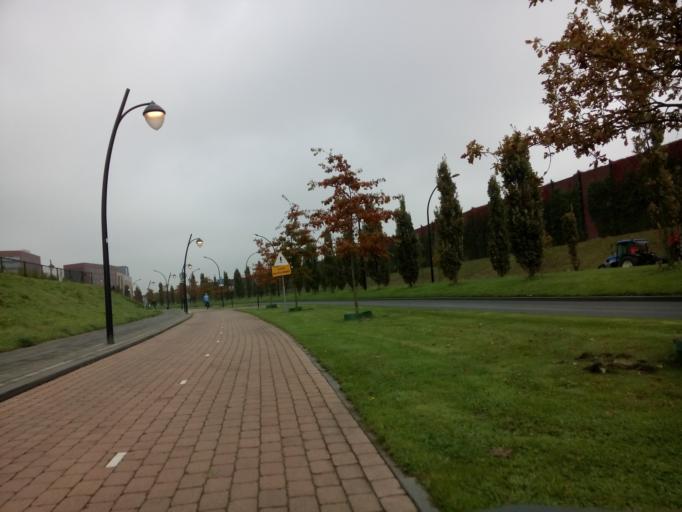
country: NL
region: Utrecht
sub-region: Gemeente Amersfoort
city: Randenbroek
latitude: 52.1861
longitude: 5.4374
